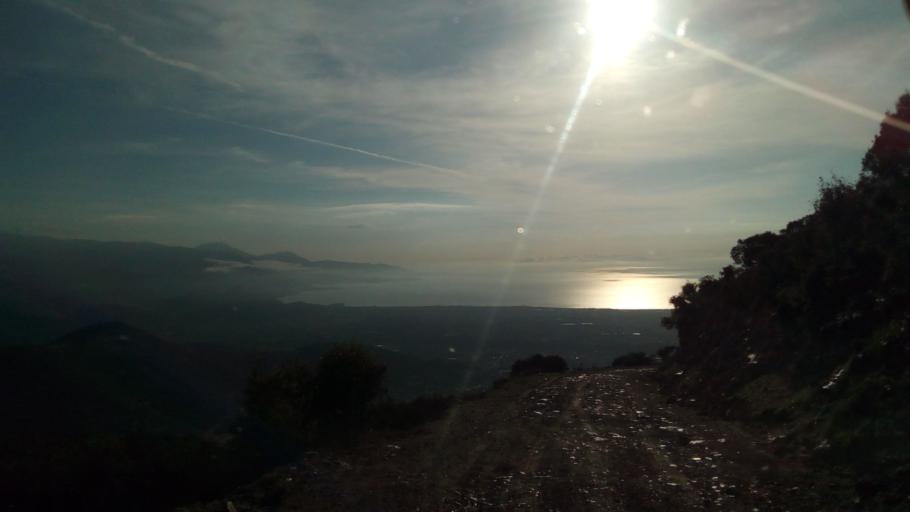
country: GR
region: West Greece
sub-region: Nomos Aitolias kai Akarnanias
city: Nafpaktos
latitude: 38.4137
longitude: 21.8210
